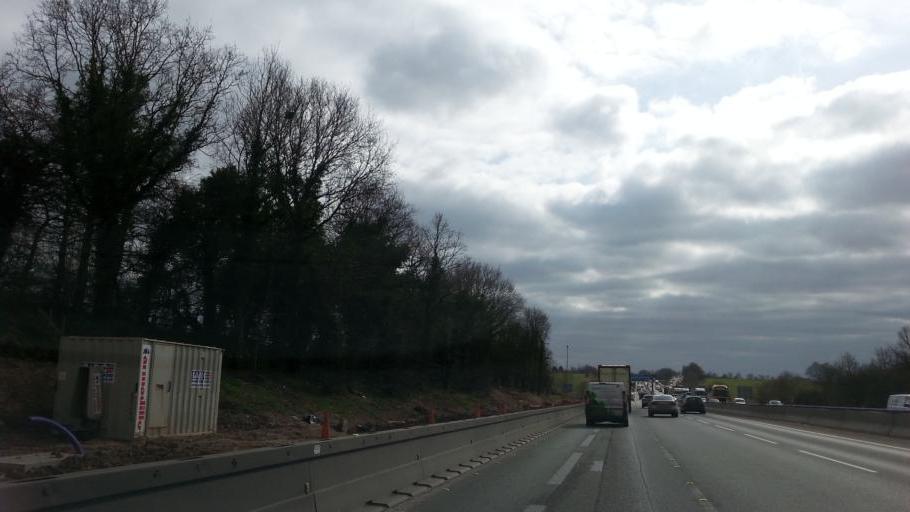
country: GB
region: England
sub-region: Cheshire East
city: Holmes Chapel
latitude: 53.2098
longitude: -2.3879
